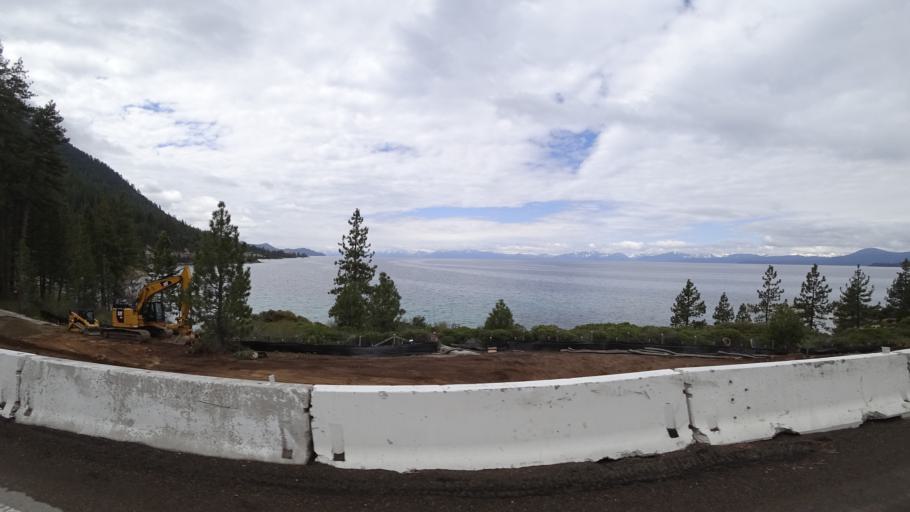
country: US
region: Nevada
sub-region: Washoe County
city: Incline Village
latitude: 39.2220
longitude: -119.9290
